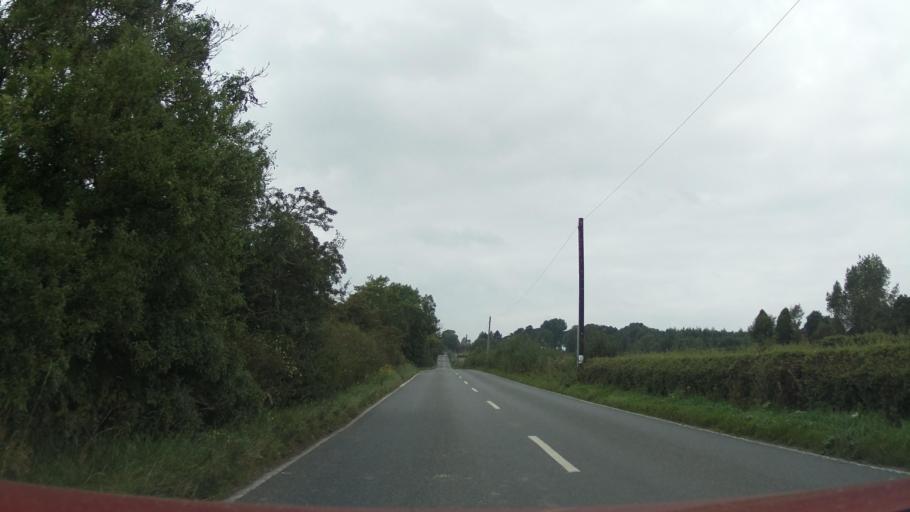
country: GB
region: England
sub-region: Derbyshire
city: Wirksworth
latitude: 53.0174
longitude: -1.5907
